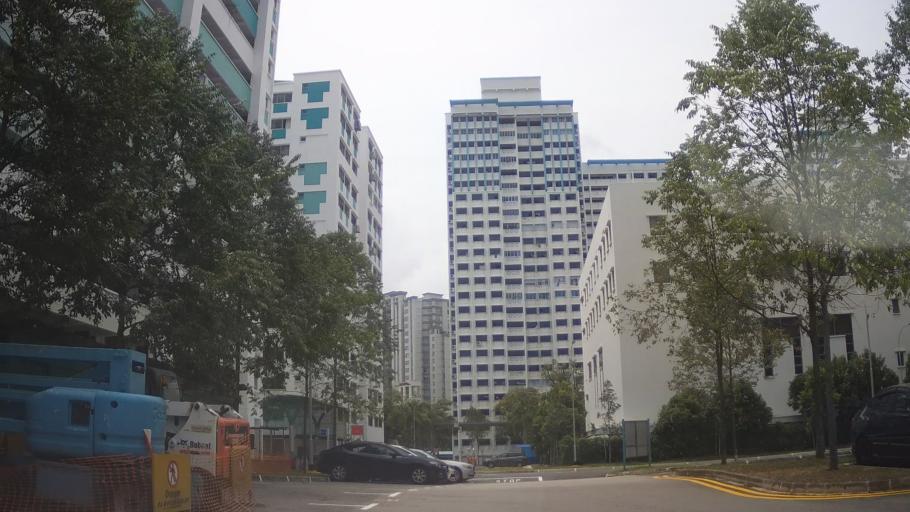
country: MY
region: Johor
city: Johor Bahru
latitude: 1.3761
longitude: 103.7666
